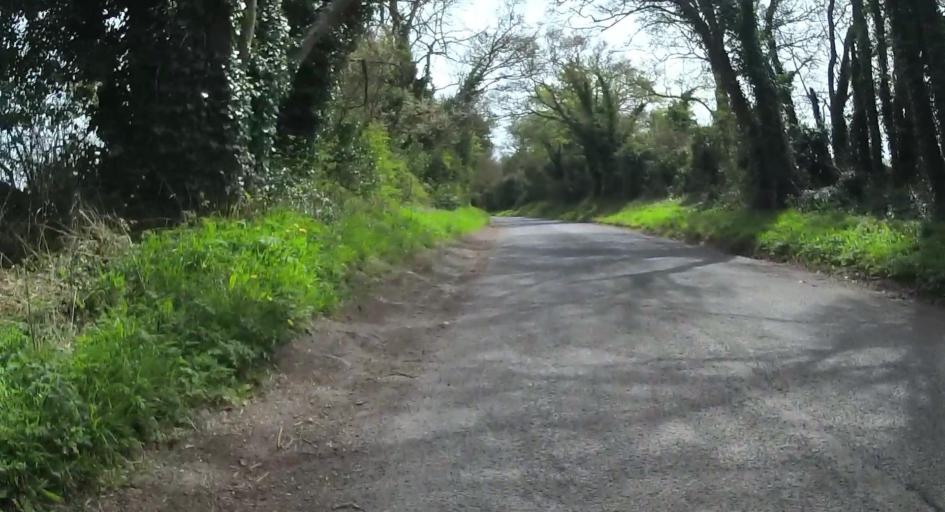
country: GB
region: England
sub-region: Hampshire
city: Alton
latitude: 51.1681
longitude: -0.9566
